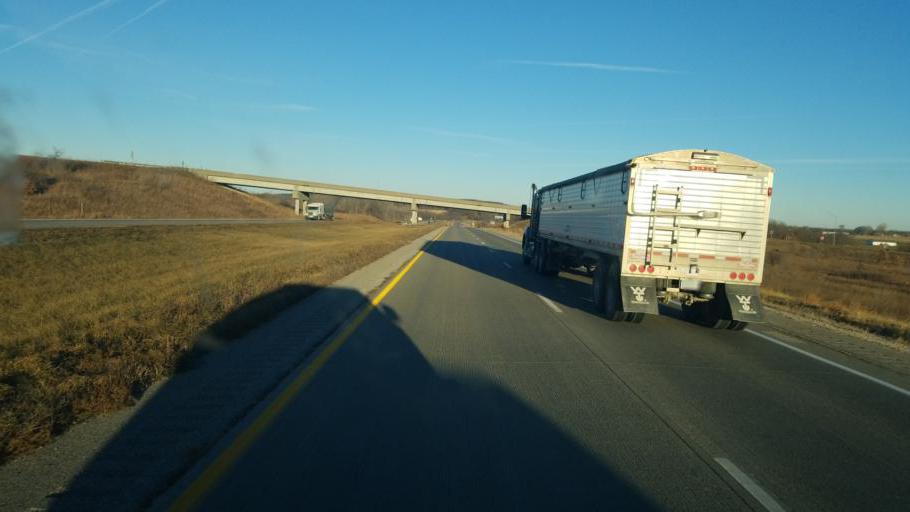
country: US
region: Iowa
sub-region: Wapello County
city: Eddyville
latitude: 41.1724
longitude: -92.6308
